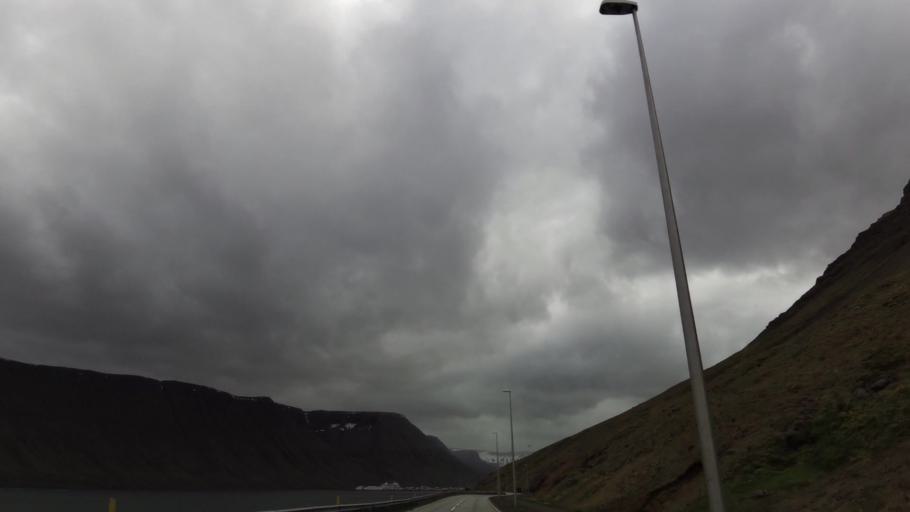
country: IS
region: Westfjords
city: Isafjoerdur
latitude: 66.0969
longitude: -23.1112
